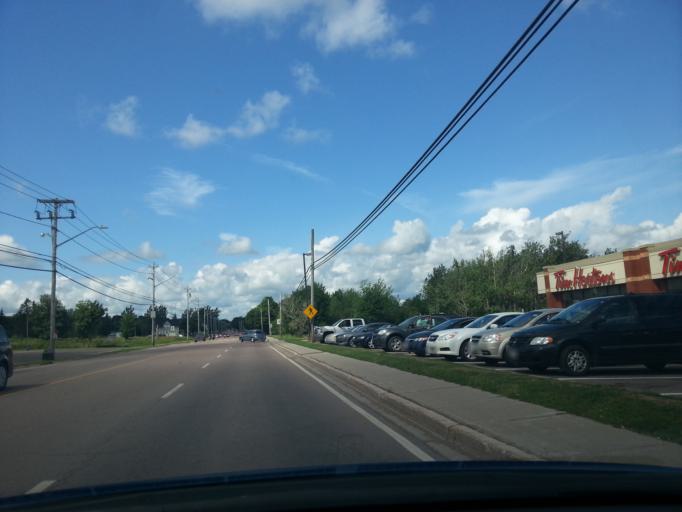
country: CA
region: New Brunswick
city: Shediac
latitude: 46.2227
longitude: -64.5216
